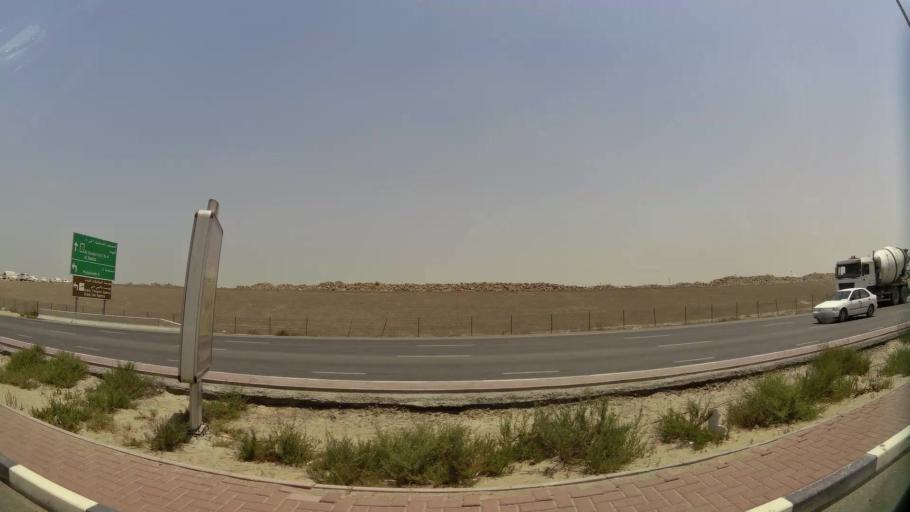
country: AE
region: Ash Shariqah
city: Sharjah
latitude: 25.2800
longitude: 55.4179
